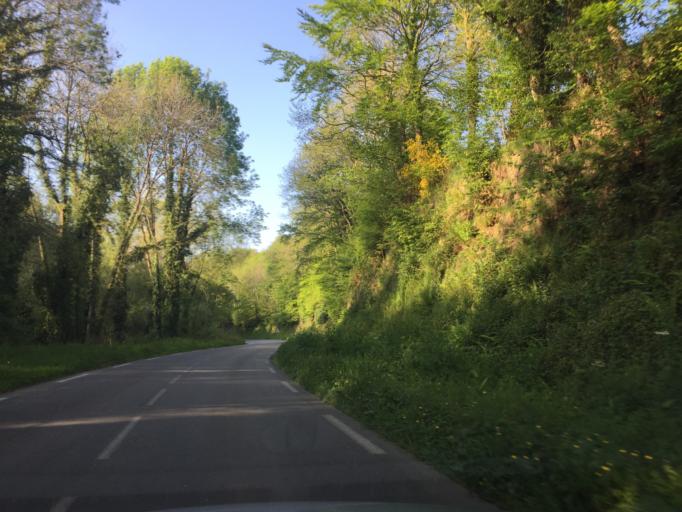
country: FR
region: Brittany
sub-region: Departement des Cotes-d'Armor
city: Crehen
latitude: 48.5719
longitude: -2.2404
